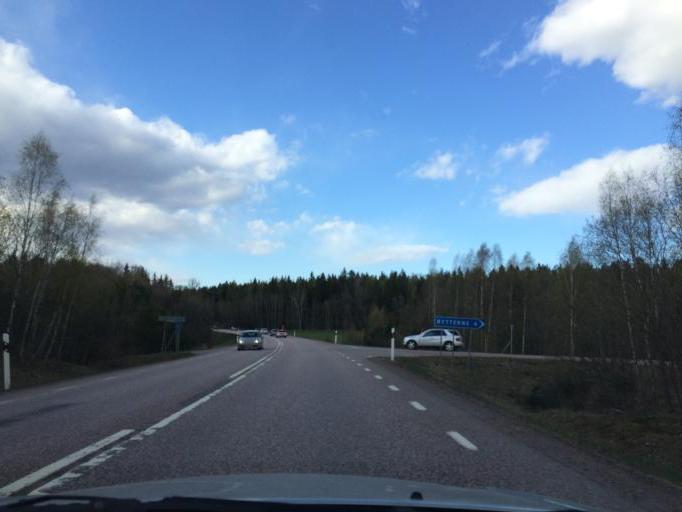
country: SE
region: Soedermanland
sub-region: Eskilstuna Kommun
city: Kvicksund
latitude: 59.5251
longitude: 16.3243
